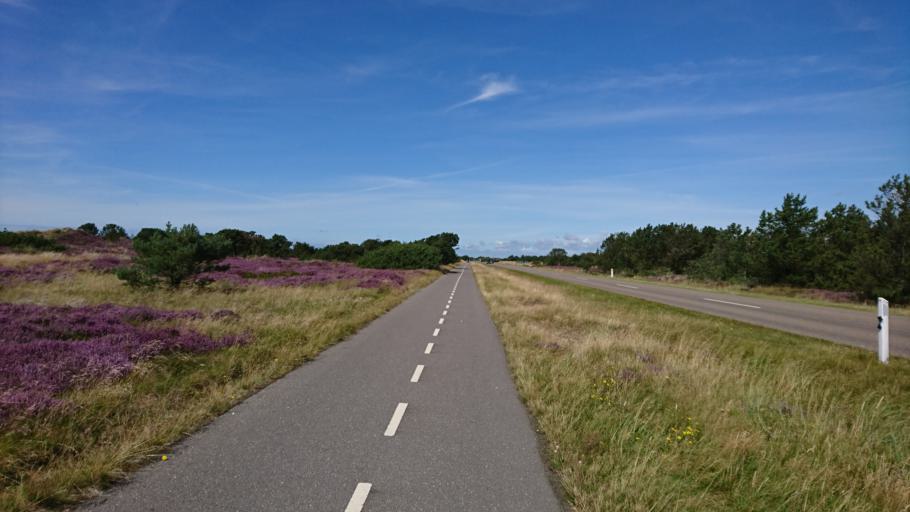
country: DK
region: South Denmark
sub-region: Fano Kommune
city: Nordby
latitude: 55.4117
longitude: 8.4094
